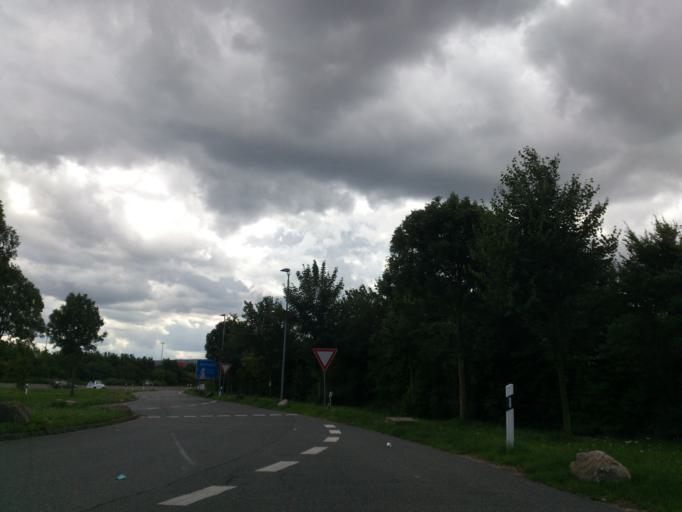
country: DE
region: Lower Saxony
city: Bad Nenndorf
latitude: 52.3467
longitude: 9.4201
